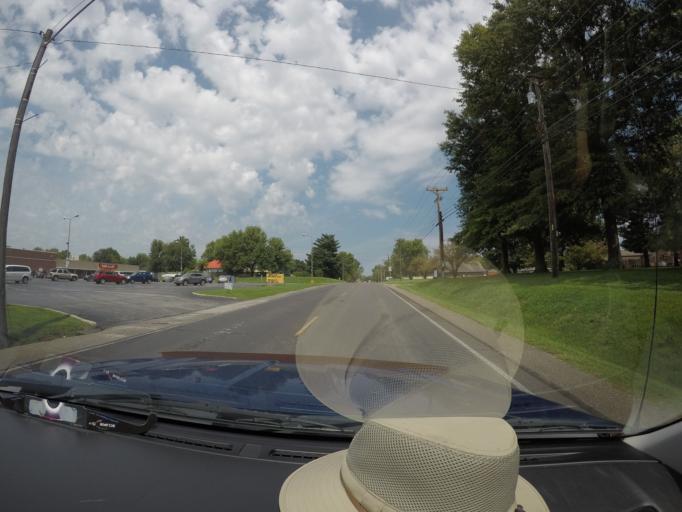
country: US
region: Missouri
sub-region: Lafayette County
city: Lexington
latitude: 39.1681
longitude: -93.8781
